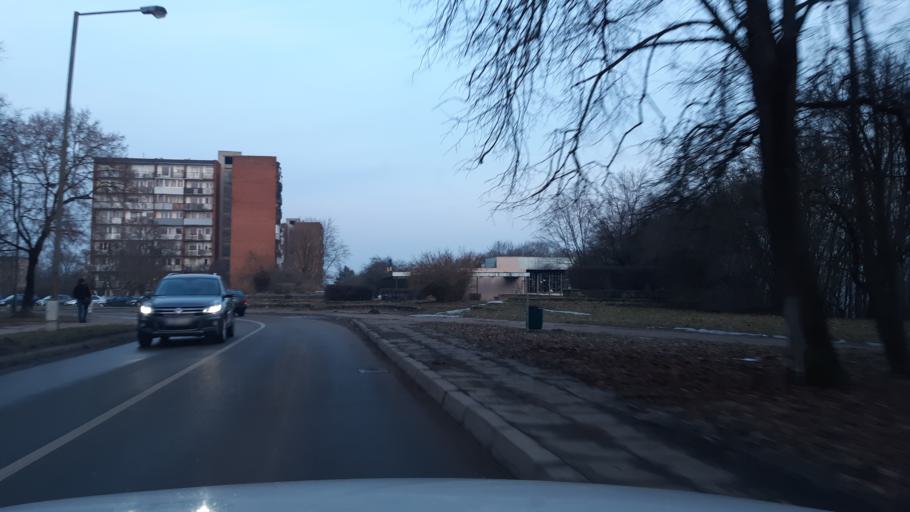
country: LT
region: Kauno apskritis
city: Dainava (Kaunas)
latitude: 54.8972
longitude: 23.9726
